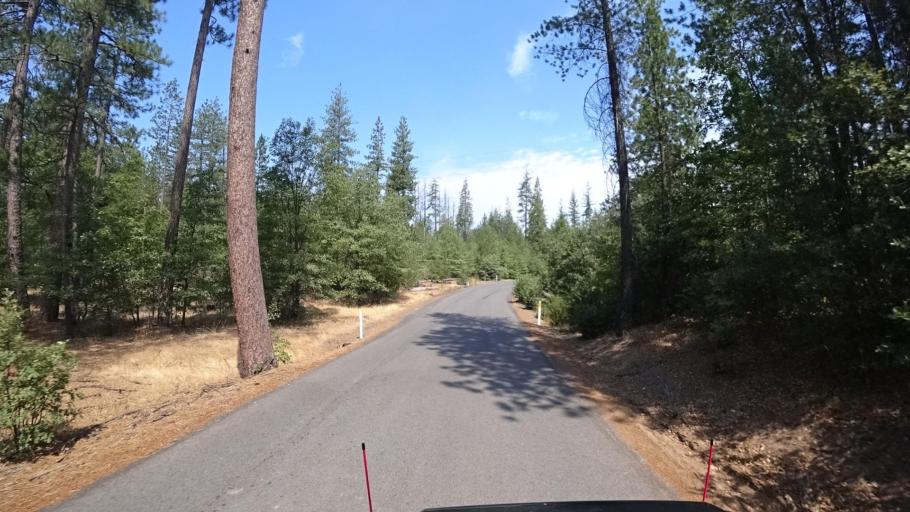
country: US
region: California
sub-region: Mariposa County
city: Midpines
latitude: 37.7093
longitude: -120.0986
